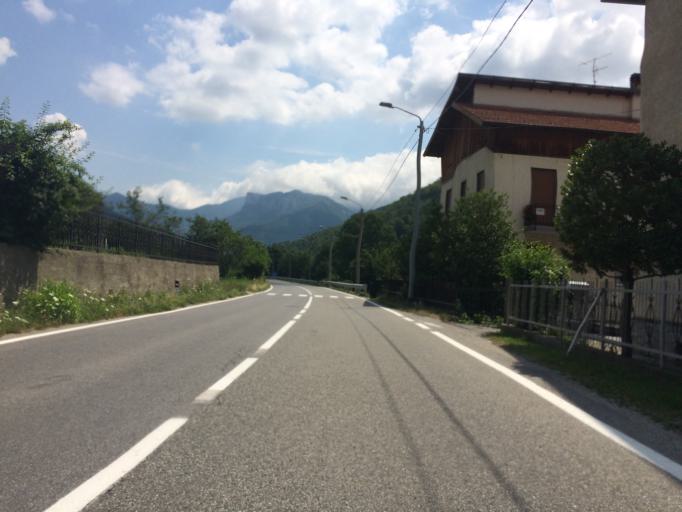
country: IT
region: Piedmont
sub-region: Provincia di Cuneo
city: Ormea
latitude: 44.1546
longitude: 7.9196
